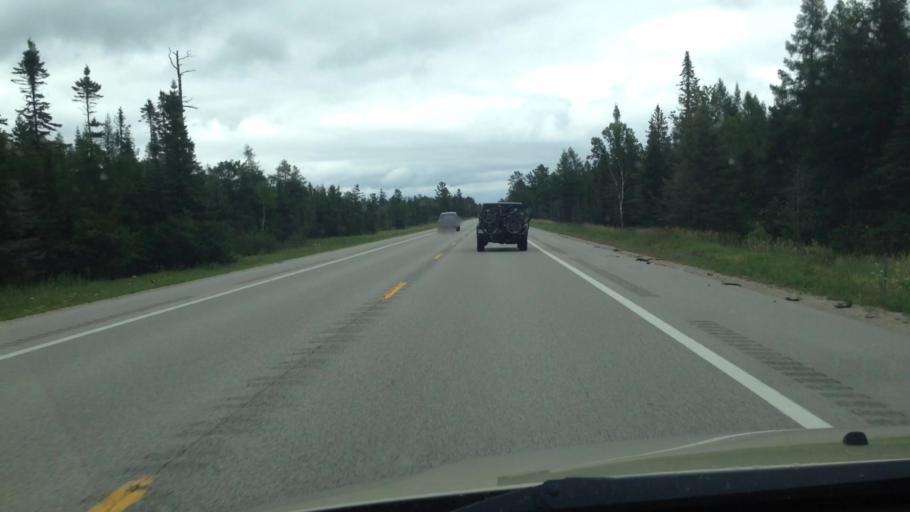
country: US
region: Michigan
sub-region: Luce County
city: Newberry
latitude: 46.1007
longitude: -85.5297
